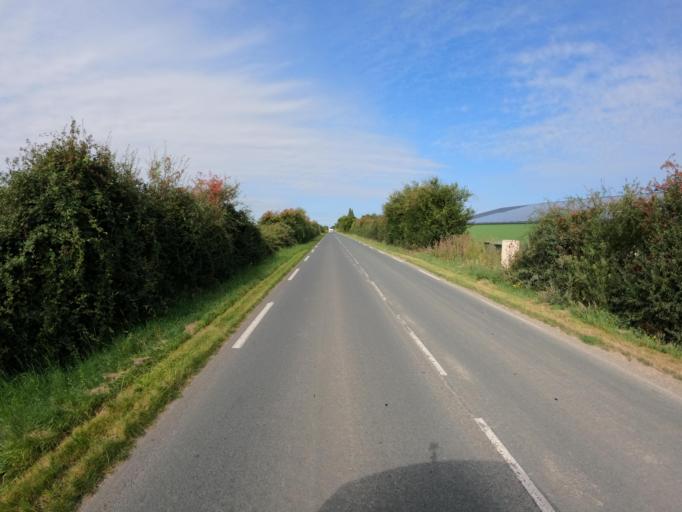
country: FR
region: Pays de la Loire
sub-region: Departement de la Vendee
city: Triaize
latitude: 46.3681
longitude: -1.2234
